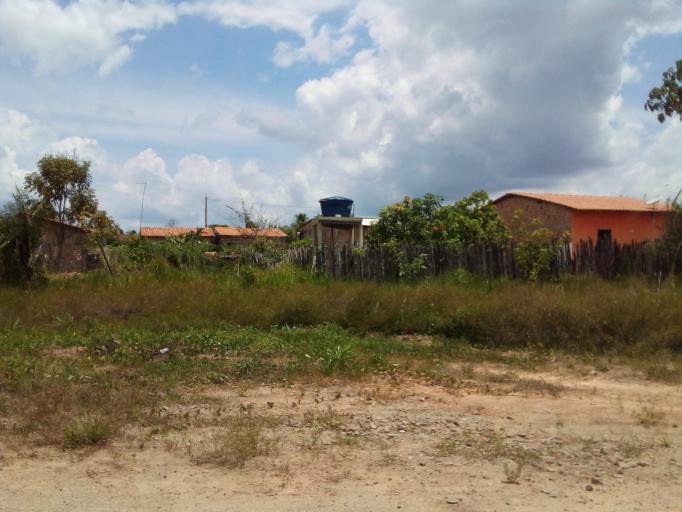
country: BR
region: Maranhao
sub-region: Itapecuru Mirim
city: Itapecuru Mirim
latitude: -3.1415
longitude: -44.3410
